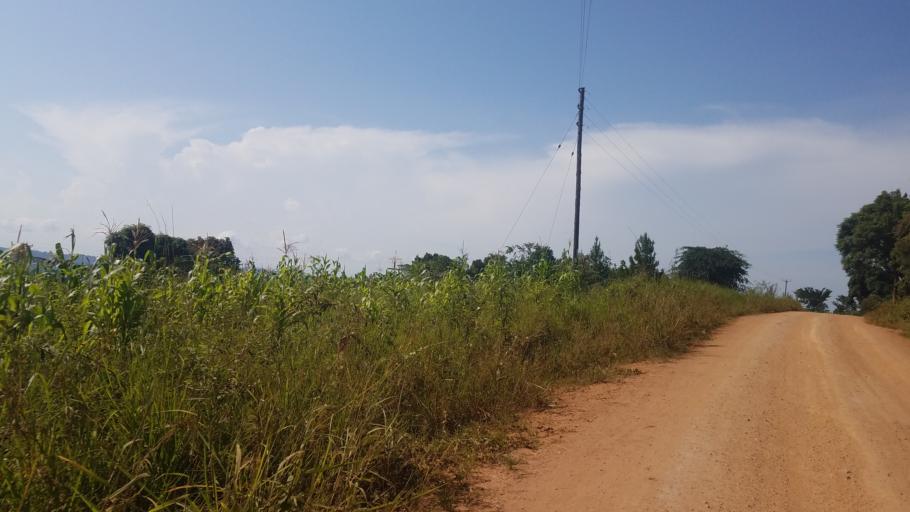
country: UG
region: Central Region
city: Masaka
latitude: -0.3033
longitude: 31.6829
